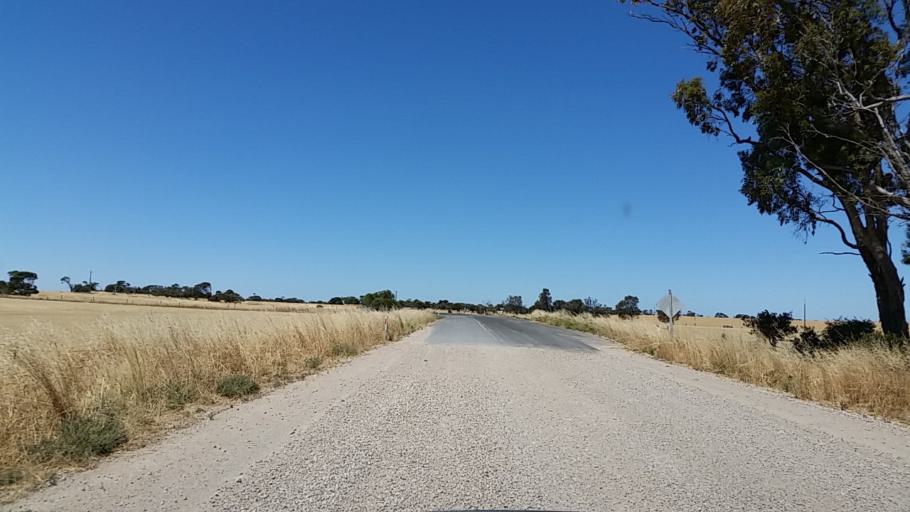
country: AU
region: South Australia
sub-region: Yorke Peninsula
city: Honiton
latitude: -35.0699
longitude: 137.5321
